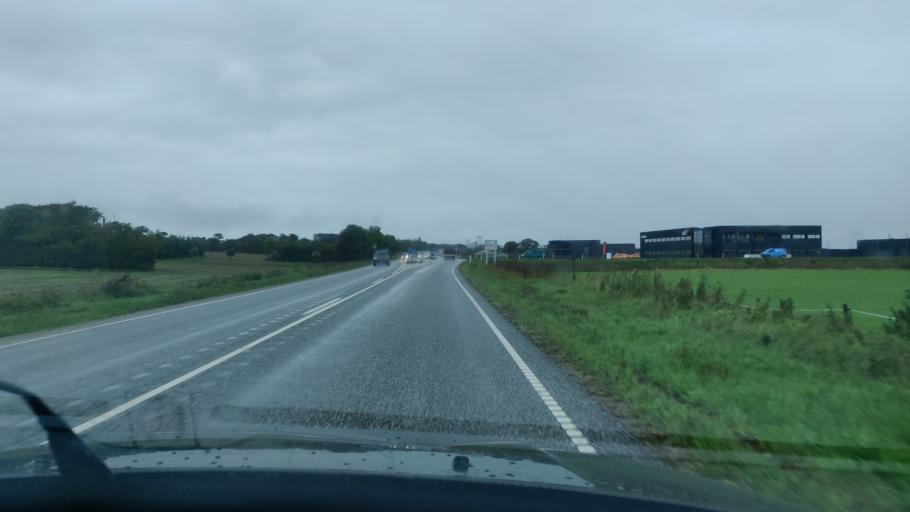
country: DK
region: North Denmark
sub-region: Thisted Kommune
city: Thisted
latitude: 56.9711
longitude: 8.7332
